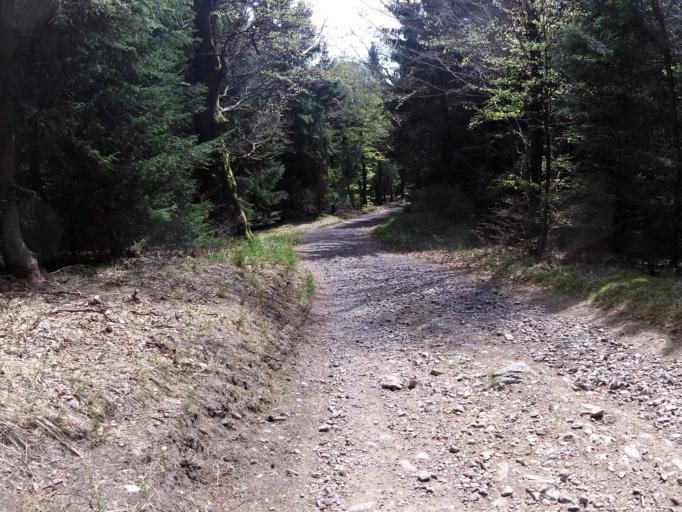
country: DE
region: Thuringia
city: Brotterode
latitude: 50.8482
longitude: 10.4173
